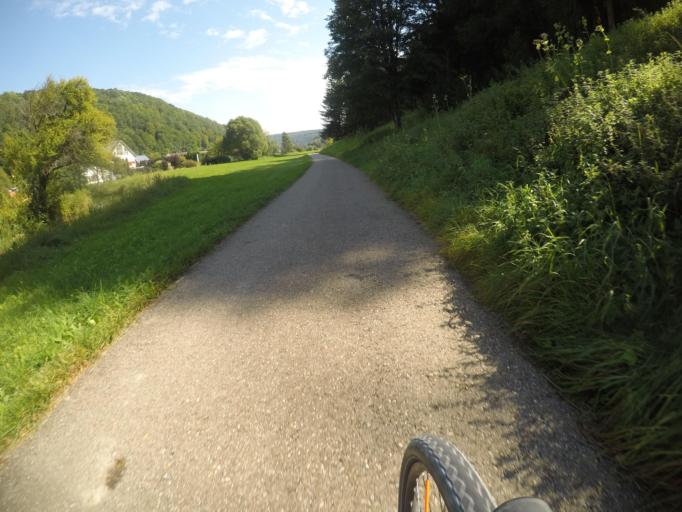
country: DE
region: Baden-Wuerttemberg
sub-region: Tuebingen Region
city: Mehrstetten
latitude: 48.3708
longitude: 9.6390
